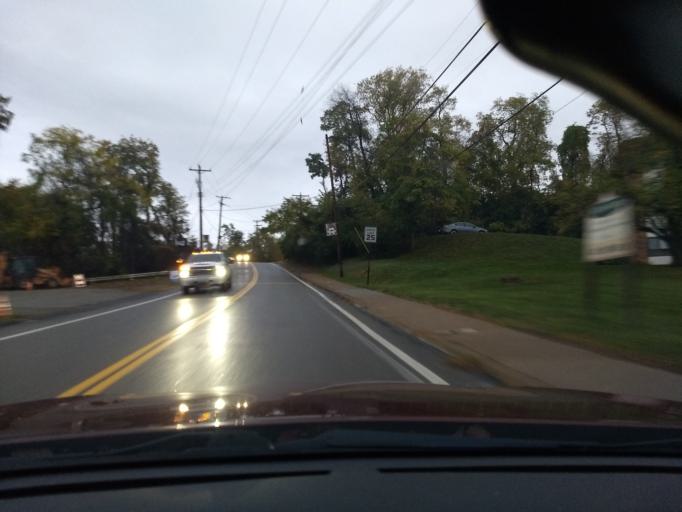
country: US
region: Pennsylvania
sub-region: Allegheny County
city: Pleasant Hills
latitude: 40.3232
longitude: -79.9566
